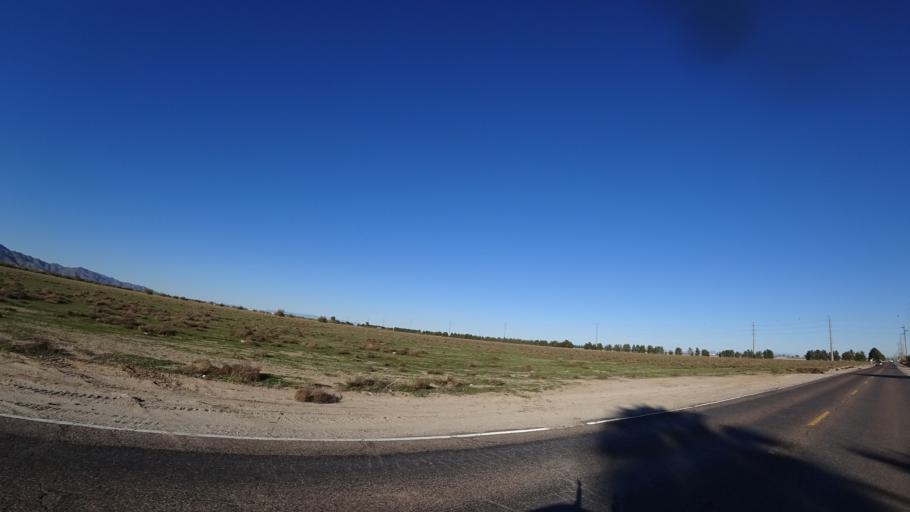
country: US
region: Arizona
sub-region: Maricopa County
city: Citrus Park
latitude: 33.4647
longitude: -112.4666
